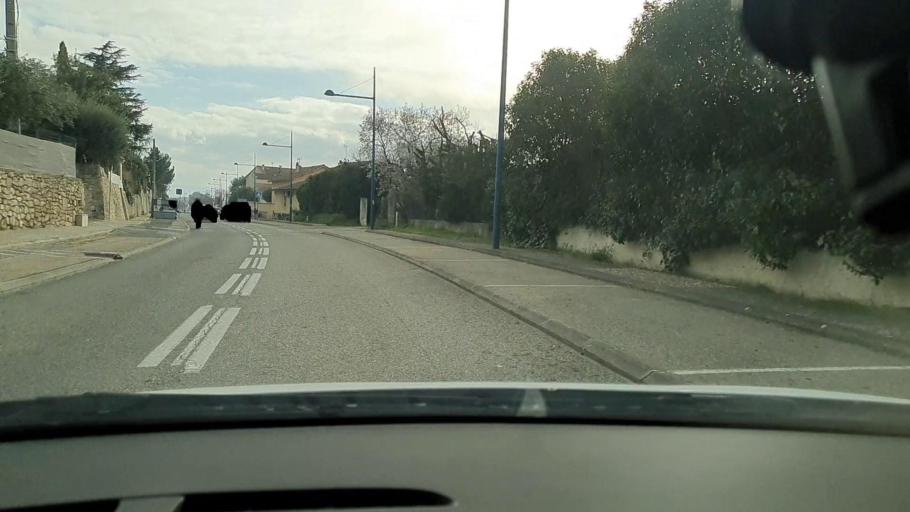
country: FR
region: Languedoc-Roussillon
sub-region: Departement du Gard
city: Beaucaire
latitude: 43.8130
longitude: 4.6326
